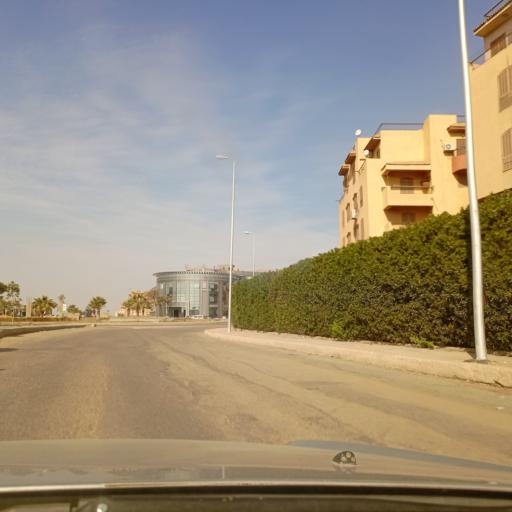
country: EG
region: Muhafazat al Qalyubiyah
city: Al Khankah
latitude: 30.0448
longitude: 31.4852
